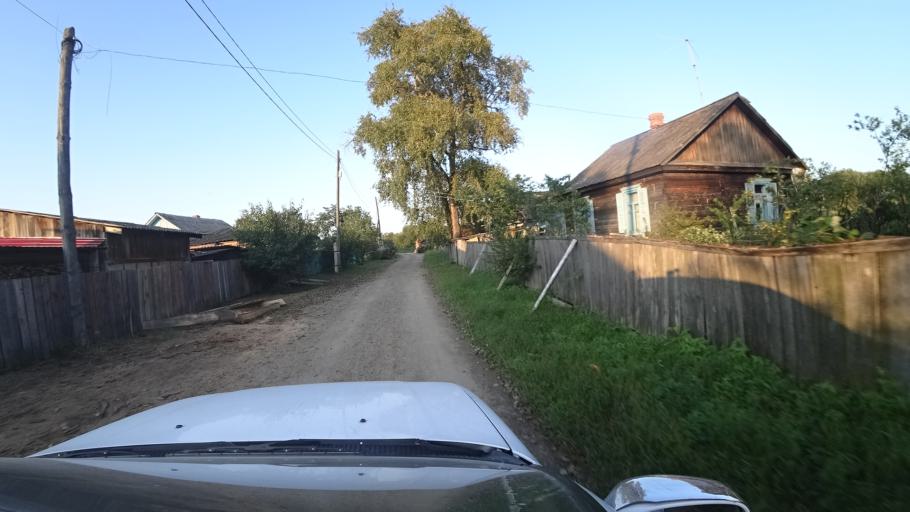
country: RU
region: Primorskiy
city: Dal'nerechensk
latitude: 45.9419
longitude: 133.7566
